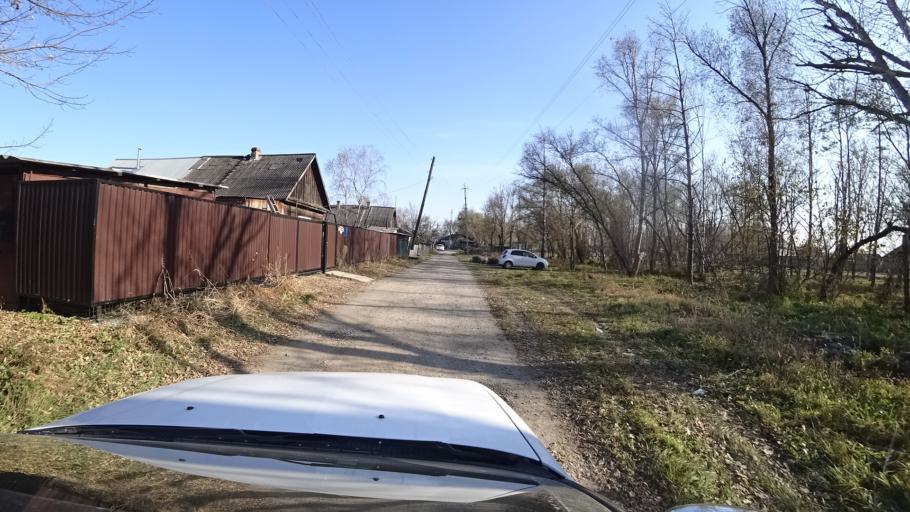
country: RU
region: Primorskiy
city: Dal'nerechensk
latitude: 45.9216
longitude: 133.7527
